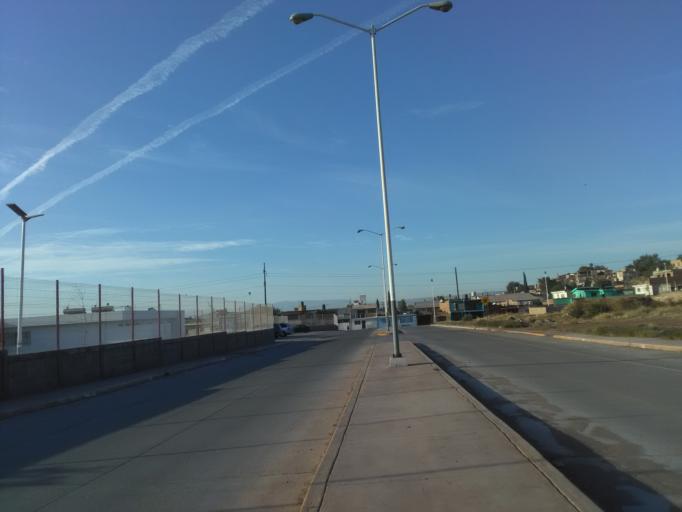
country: MX
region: Durango
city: Victoria de Durango
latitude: 24.0480
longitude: -104.6633
